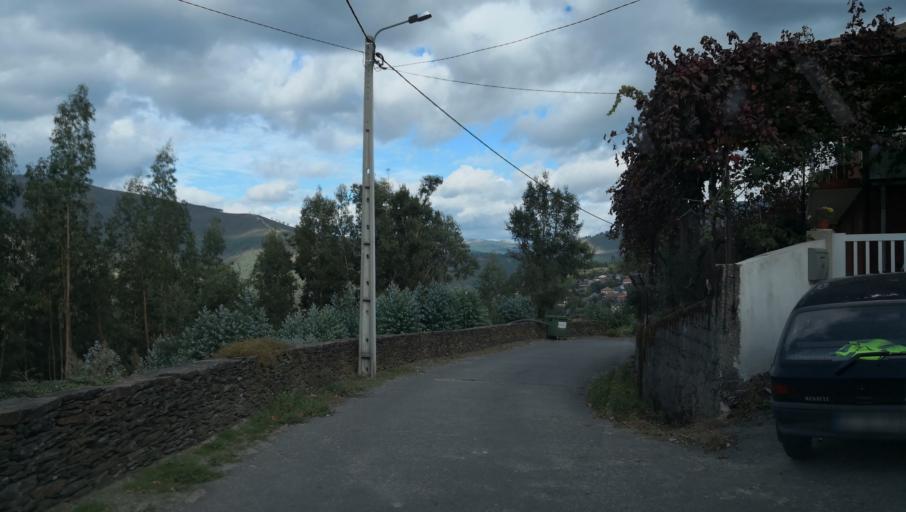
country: PT
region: Vila Real
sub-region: Mondim de Basto
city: Mondim de Basto
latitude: 41.3550
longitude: -7.8912
